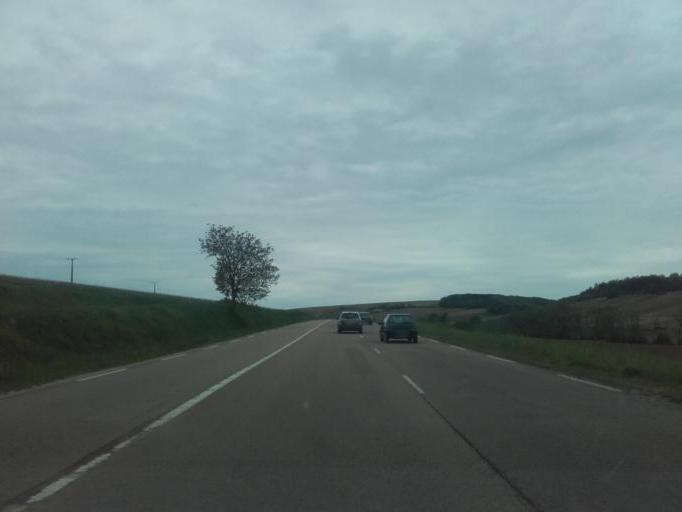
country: FR
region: Bourgogne
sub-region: Departement de l'Yonne
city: Chablis
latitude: 47.8234
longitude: 3.7607
